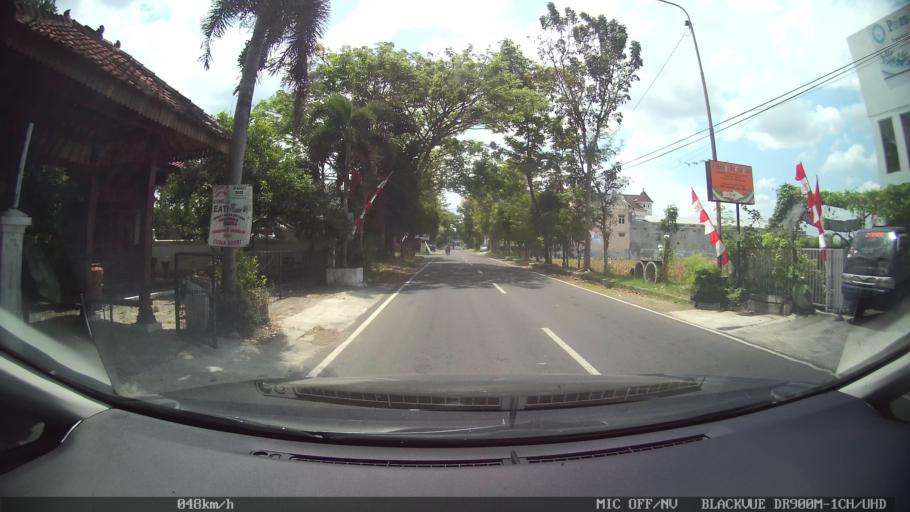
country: ID
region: Daerah Istimewa Yogyakarta
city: Bantul
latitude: -7.8832
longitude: 110.3358
